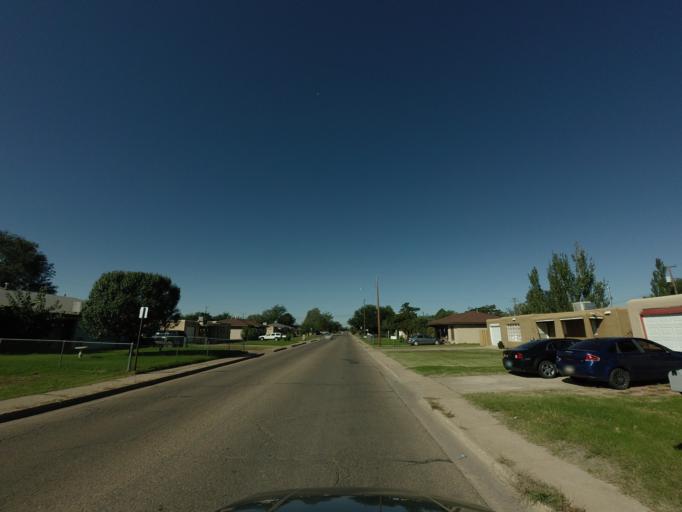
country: US
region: New Mexico
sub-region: Curry County
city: Clovis
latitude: 34.4270
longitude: -103.2082
